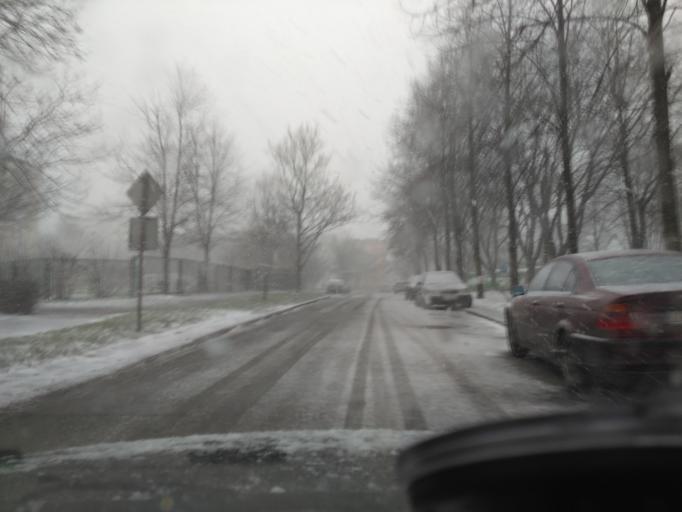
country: PL
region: Lublin Voivodeship
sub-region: Powiat lubelski
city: Lublin
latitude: 51.2306
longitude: 22.5882
